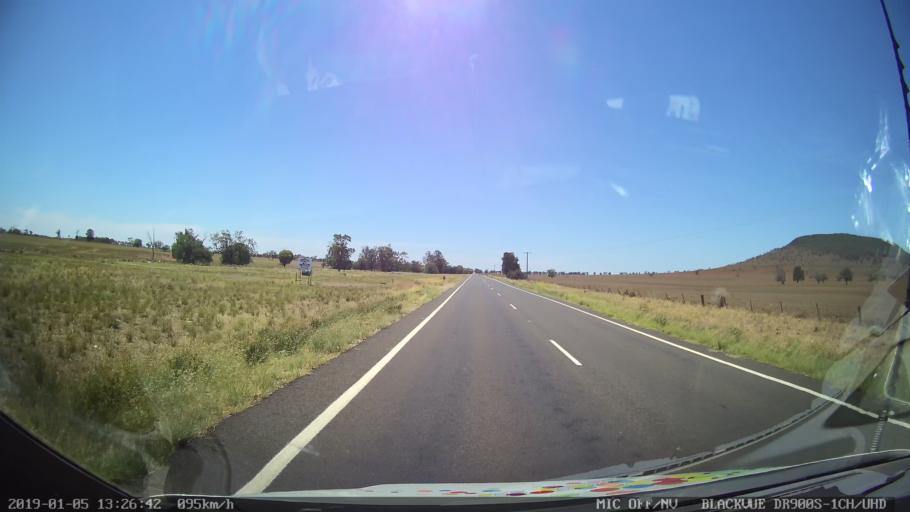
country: AU
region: New South Wales
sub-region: Gunnedah
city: Gunnedah
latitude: -31.0507
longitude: 150.0193
